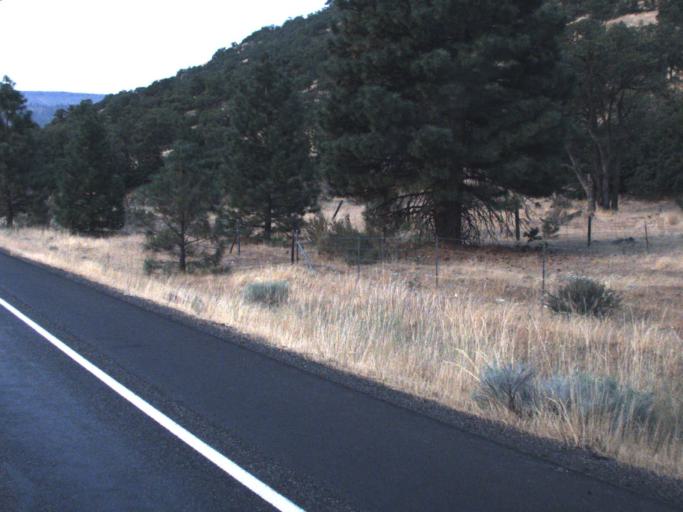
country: US
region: Washington
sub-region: Klickitat County
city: Goldendale
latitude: 46.0609
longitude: -120.5653
